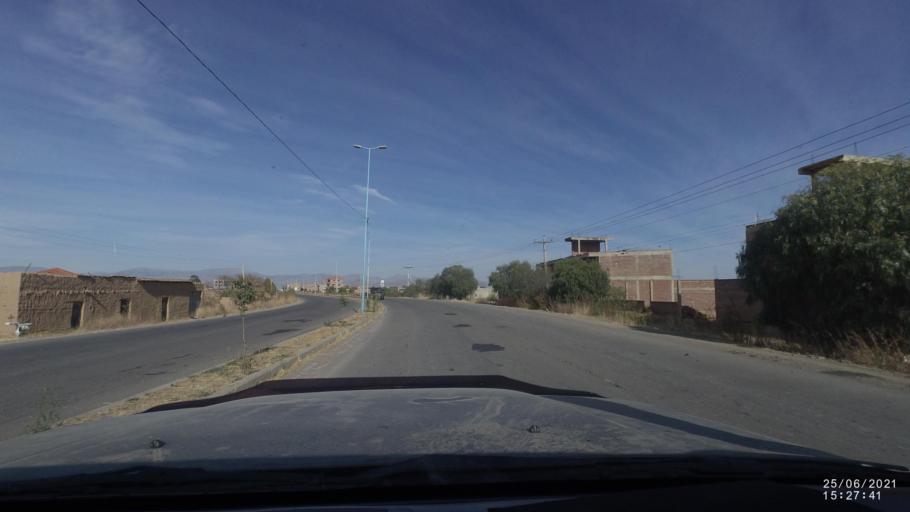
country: BO
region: Cochabamba
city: Cliza
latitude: -17.5532
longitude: -65.9470
